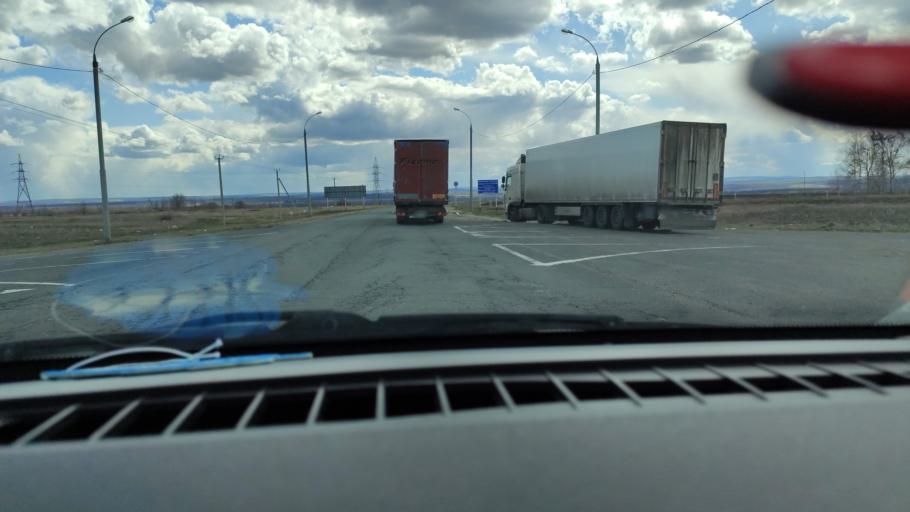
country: RU
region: Samara
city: Varlamovo
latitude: 53.1860
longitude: 48.2906
